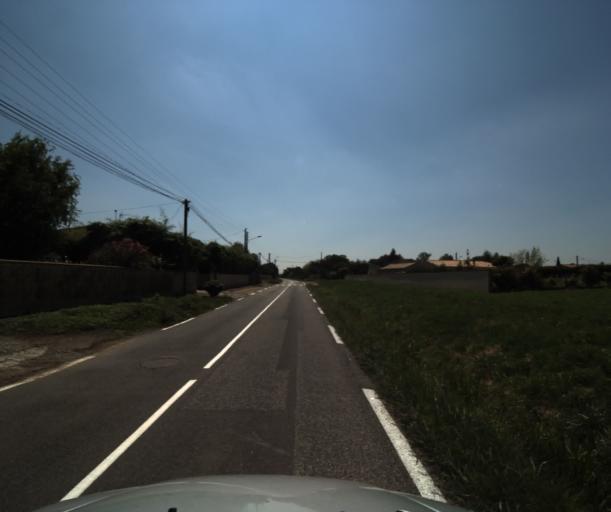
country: FR
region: Midi-Pyrenees
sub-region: Departement de la Haute-Garonne
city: Labastidette
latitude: 43.4401
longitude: 1.2582
